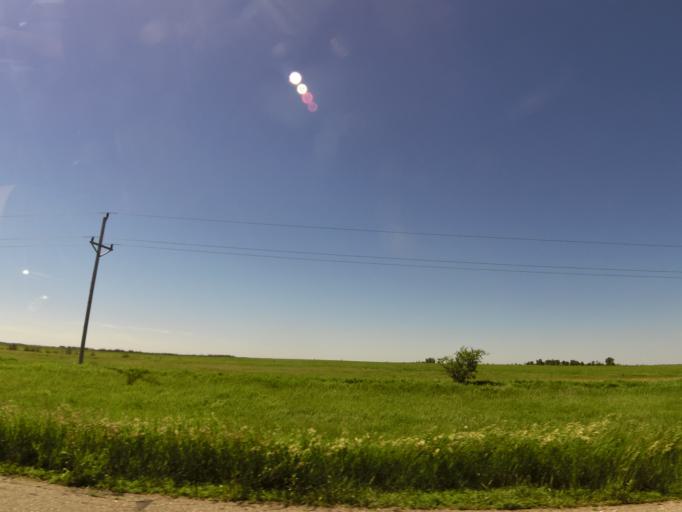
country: US
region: Minnesota
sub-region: Red Lake County
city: Red Lake Falls
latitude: 47.7602
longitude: -96.3299
